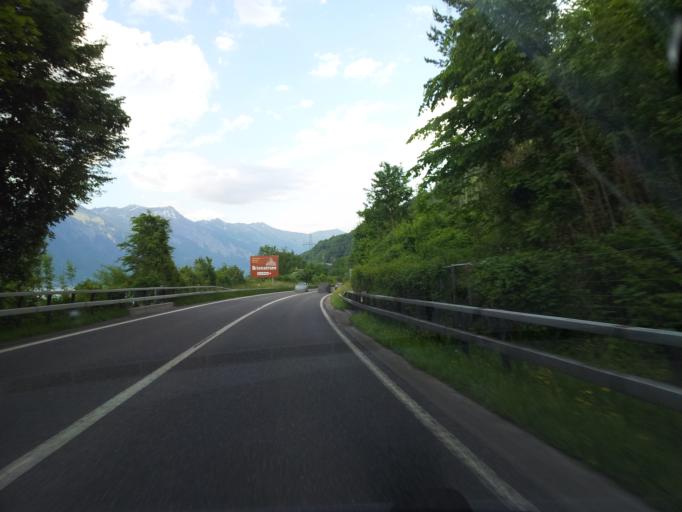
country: CH
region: Bern
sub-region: Interlaken-Oberhasli District
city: Bonigen
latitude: 46.6896
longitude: 7.9224
